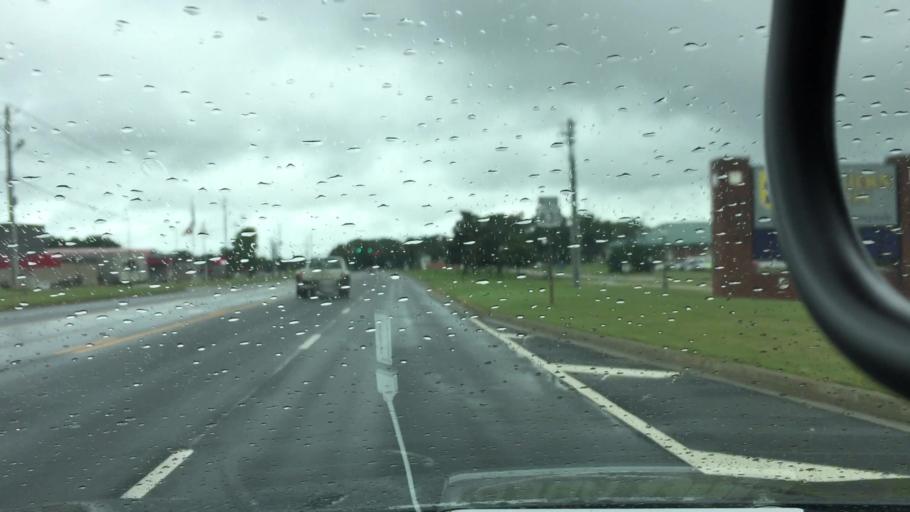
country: US
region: Alabama
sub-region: Lee County
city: Opelika
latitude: 32.6672
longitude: -85.3673
